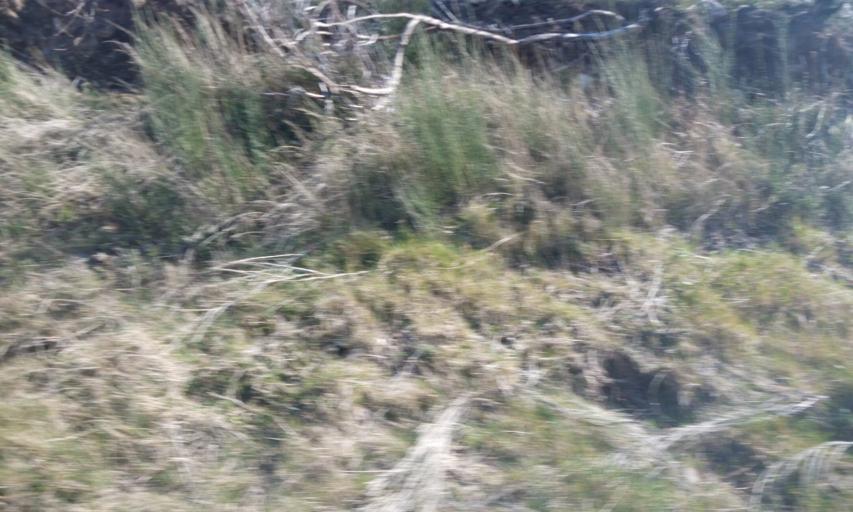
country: PT
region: Guarda
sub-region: Manteigas
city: Manteigas
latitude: 40.4900
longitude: -7.5501
